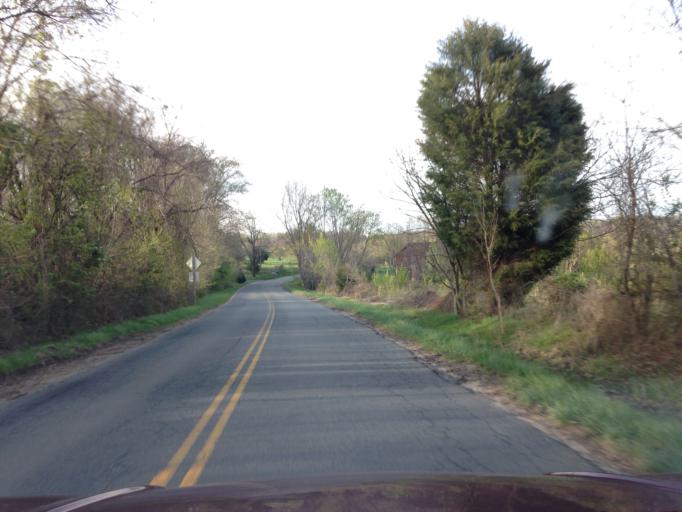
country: US
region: Maryland
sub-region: Frederick County
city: Point of Rocks
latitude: 39.2204
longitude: -77.5488
